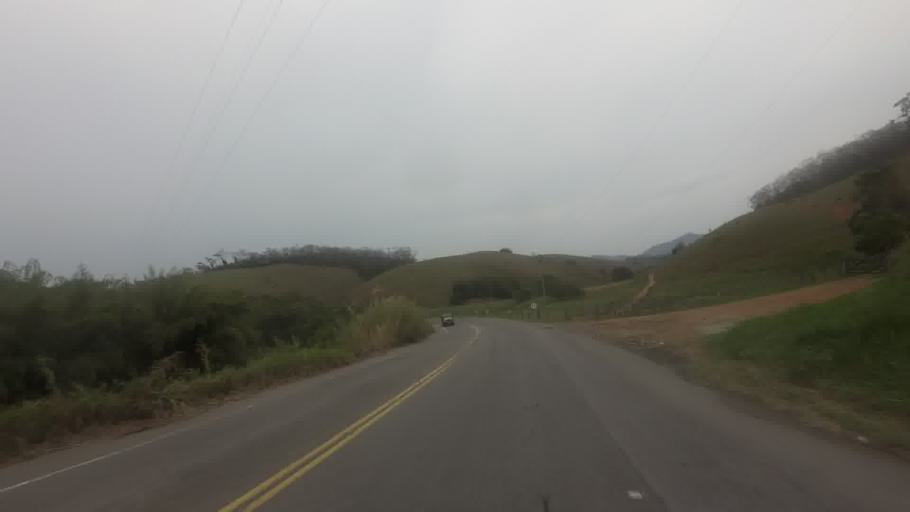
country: BR
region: Rio de Janeiro
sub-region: Santo Antonio De Padua
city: Santo Antonio de Padua
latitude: -21.6550
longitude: -42.3008
